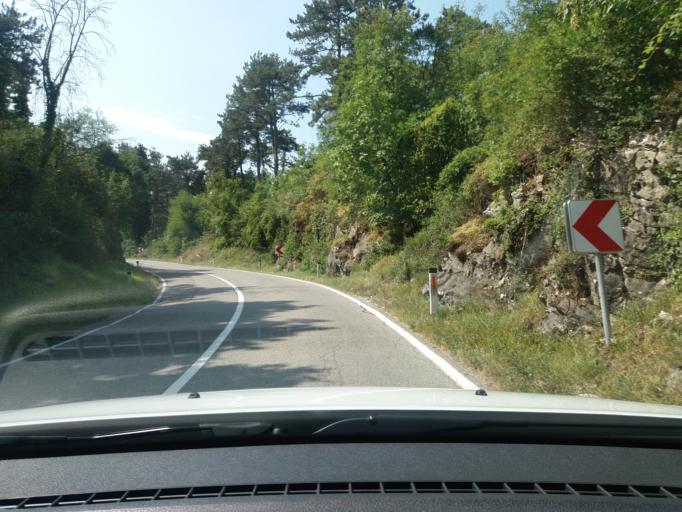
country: SI
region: Miren-Kostanjevica
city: Miren
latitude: 45.8782
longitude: 13.5937
